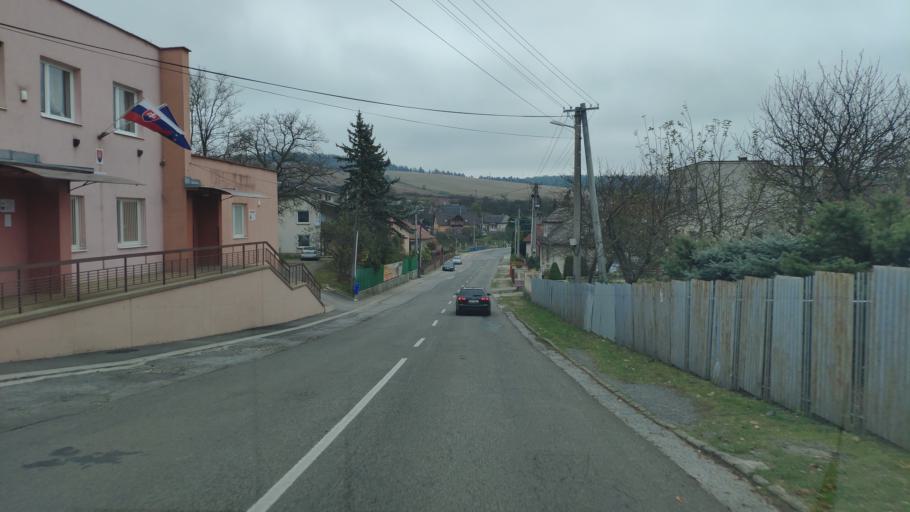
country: SK
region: Presovsky
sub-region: Okres Presov
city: Presov
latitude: 49.1196
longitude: 21.2486
